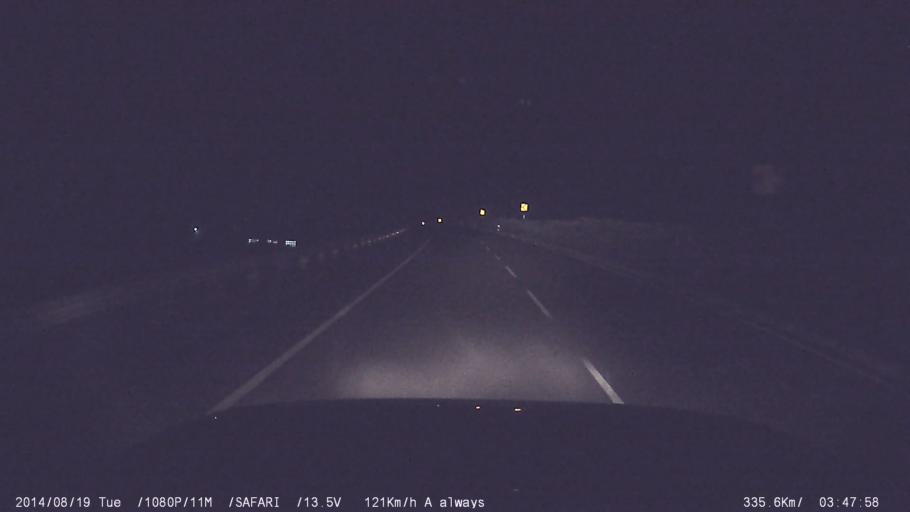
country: IN
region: Tamil Nadu
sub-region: Erode
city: Vijayapuri
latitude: 11.2381
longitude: 77.5003
